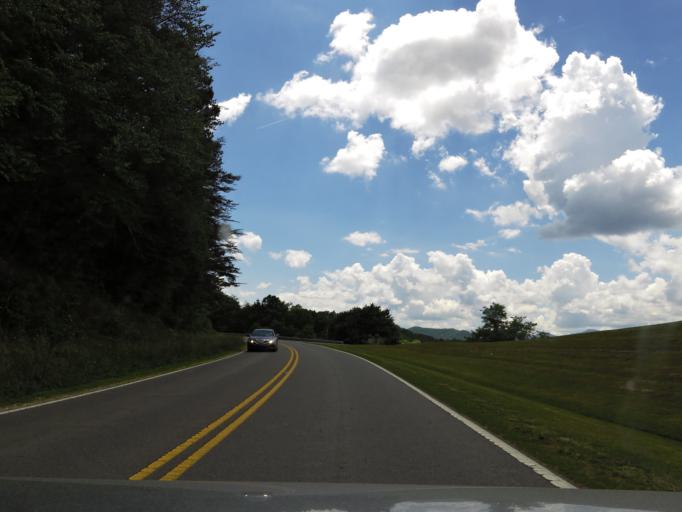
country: US
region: North Carolina
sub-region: Graham County
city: Robbinsville
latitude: 35.3609
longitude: -83.8423
